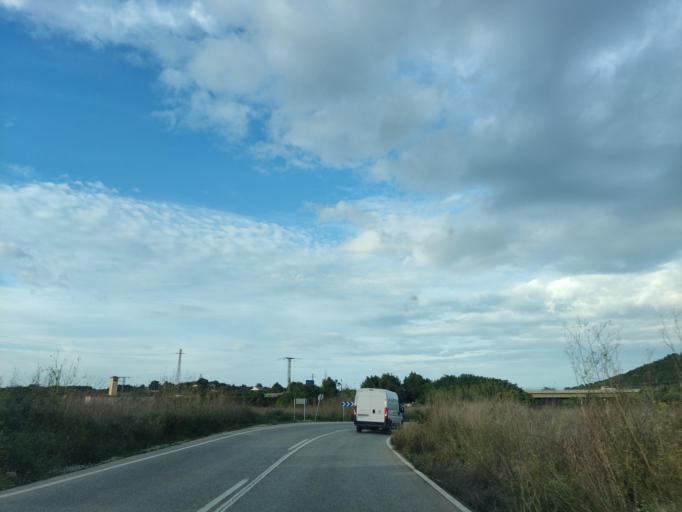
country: ES
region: Valencia
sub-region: Provincia de Alicante
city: Pedreguer
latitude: 38.8025
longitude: 0.0327
